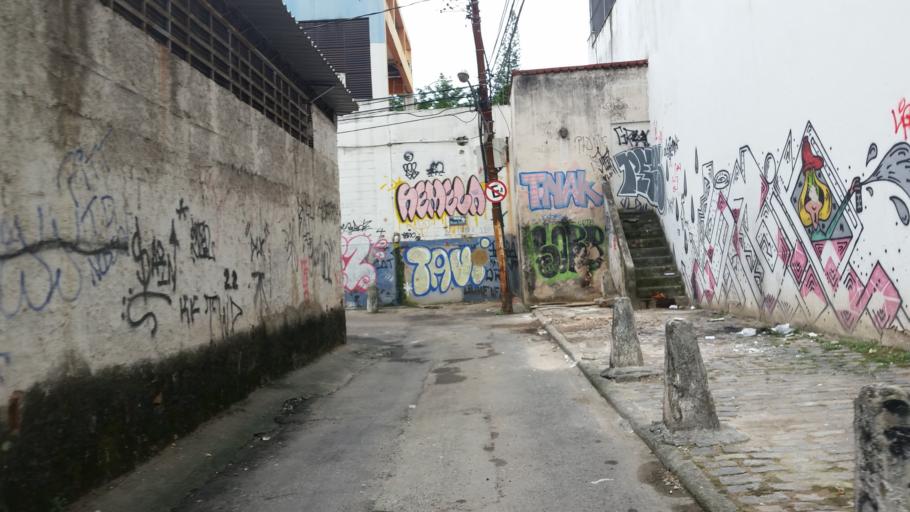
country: BR
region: Rio de Janeiro
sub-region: Rio De Janeiro
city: Rio de Janeiro
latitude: -22.9355
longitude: -43.1779
